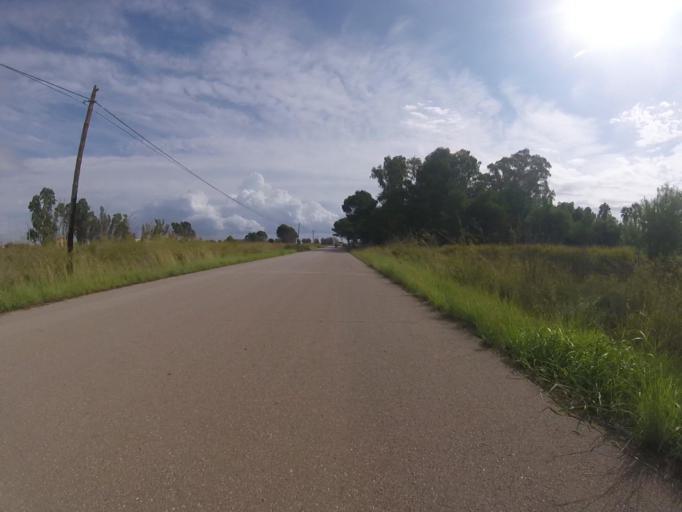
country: ES
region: Valencia
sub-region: Provincia de Castello
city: Orpesa/Oropesa del Mar
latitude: 40.1323
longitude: 0.1616
